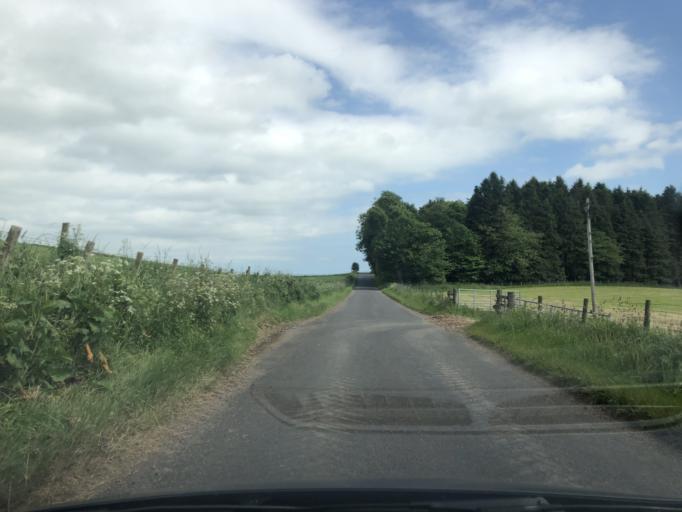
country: GB
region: Scotland
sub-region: Angus
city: Kirriemuir
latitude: 56.7244
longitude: -2.9710
